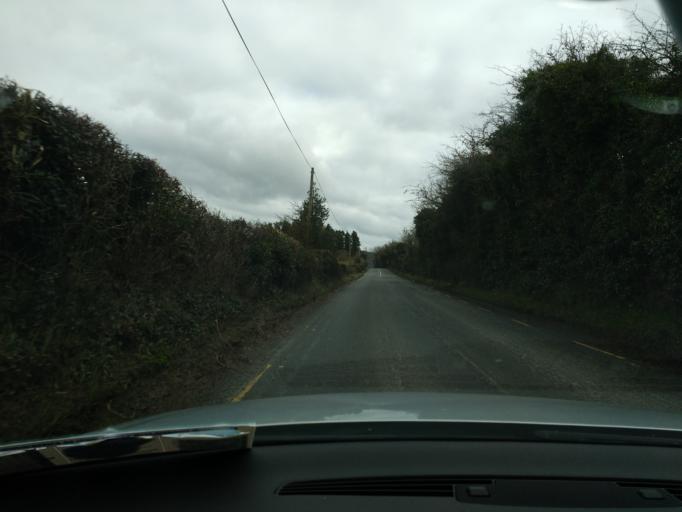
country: IE
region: Leinster
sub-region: Laois
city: Rathdowney
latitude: 52.7226
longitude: -7.5546
